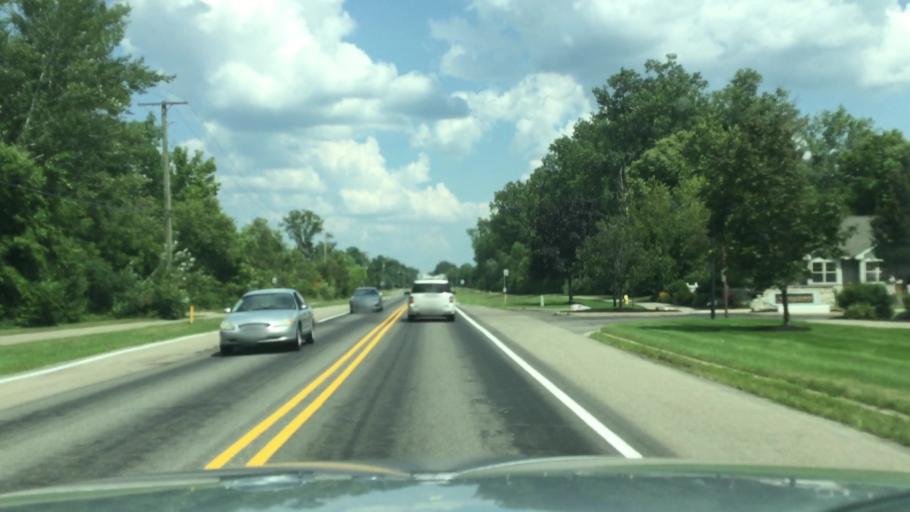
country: US
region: Michigan
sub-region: Washtenaw County
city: Ypsilanti
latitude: 42.2028
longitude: -83.5779
